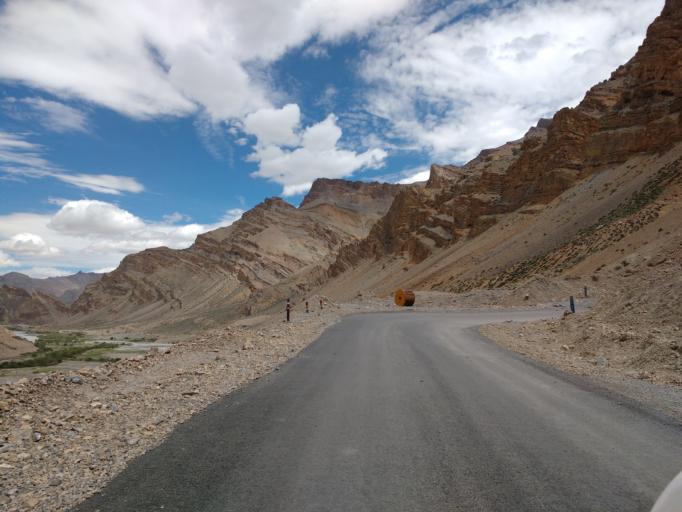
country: IN
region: Himachal Pradesh
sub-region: Lahul and Spiti
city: Kyelang
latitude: 33.0407
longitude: 77.5909
